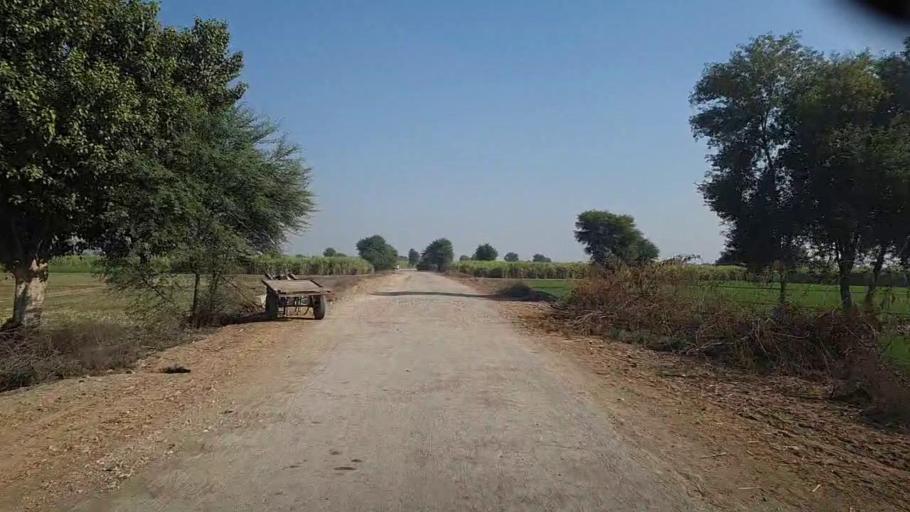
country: PK
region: Sindh
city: Darya Khan Marri
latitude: 26.6702
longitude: 68.3290
